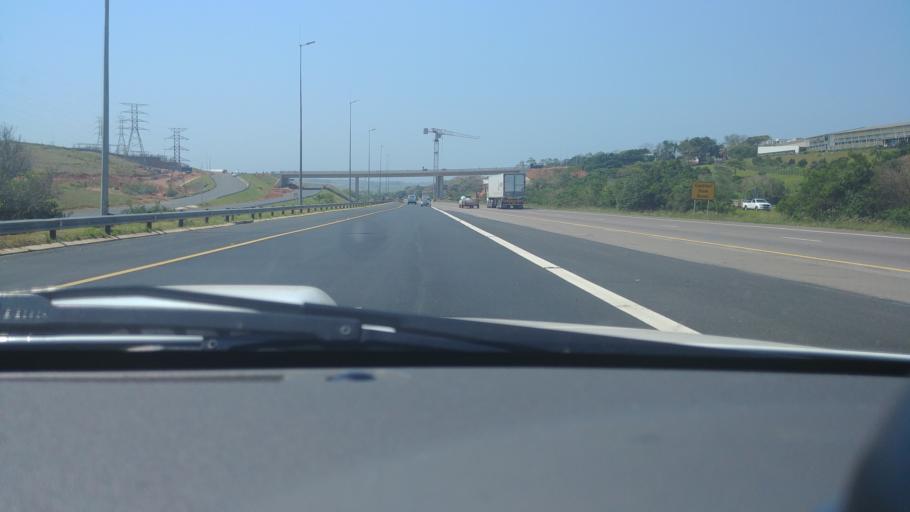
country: ZA
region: KwaZulu-Natal
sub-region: eThekwini Metropolitan Municipality
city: Durban
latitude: -29.7184
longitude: 31.0609
